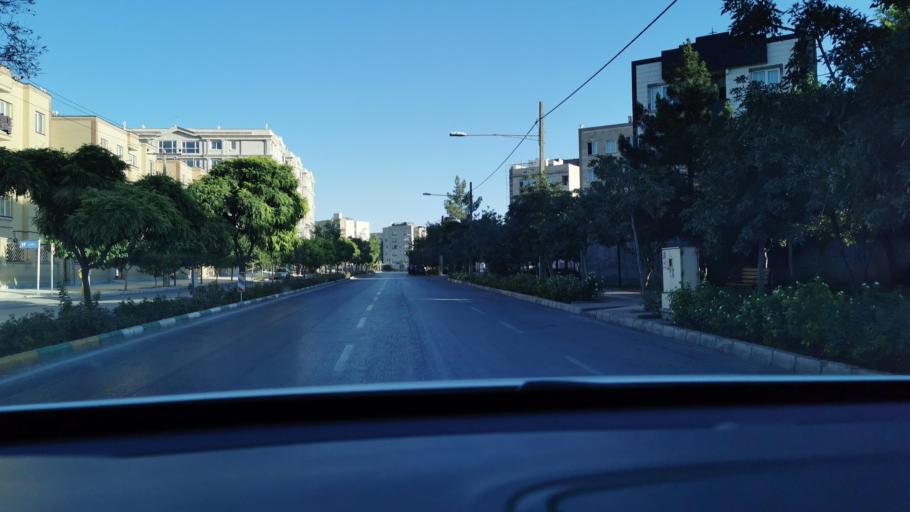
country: IR
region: Razavi Khorasan
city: Mashhad
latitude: 36.3590
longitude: 59.4848
